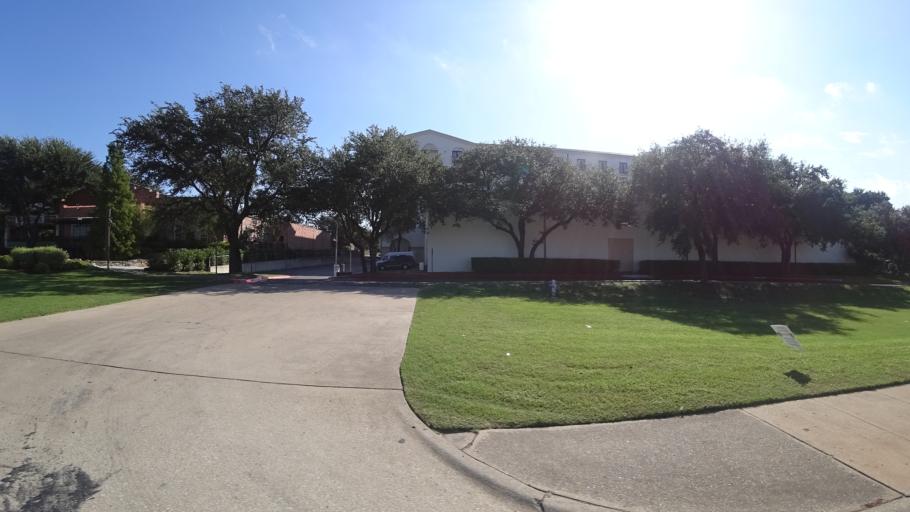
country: US
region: Texas
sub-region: Travis County
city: Austin
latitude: 30.3265
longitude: -97.7055
